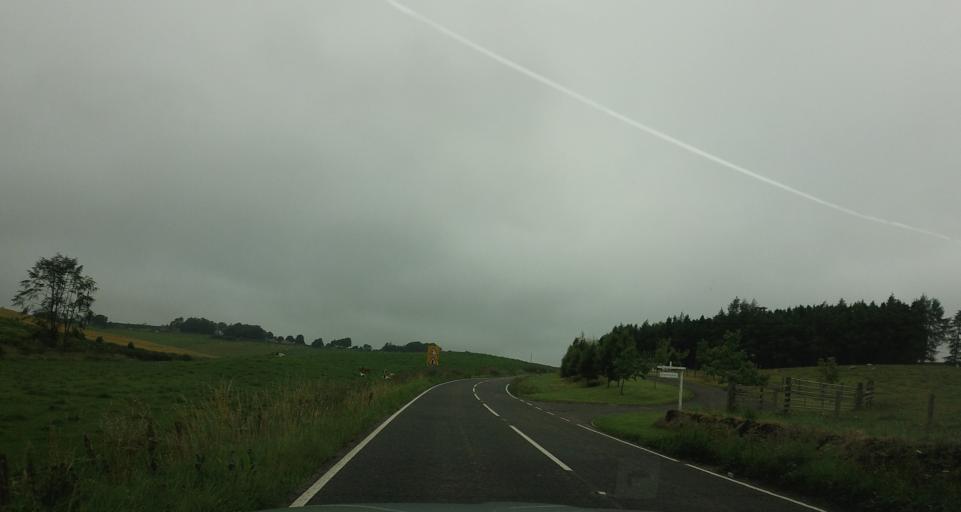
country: GB
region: Scotland
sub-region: Perth and Kinross
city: Abernethy
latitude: 56.2788
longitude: -3.3469
